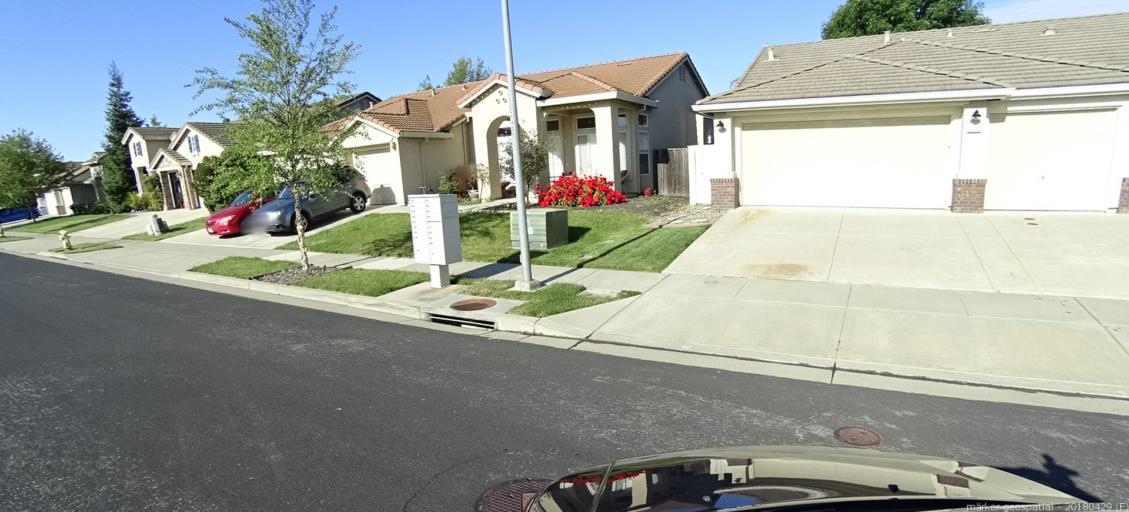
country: US
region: California
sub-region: Yolo County
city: West Sacramento
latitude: 38.5363
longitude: -121.5688
